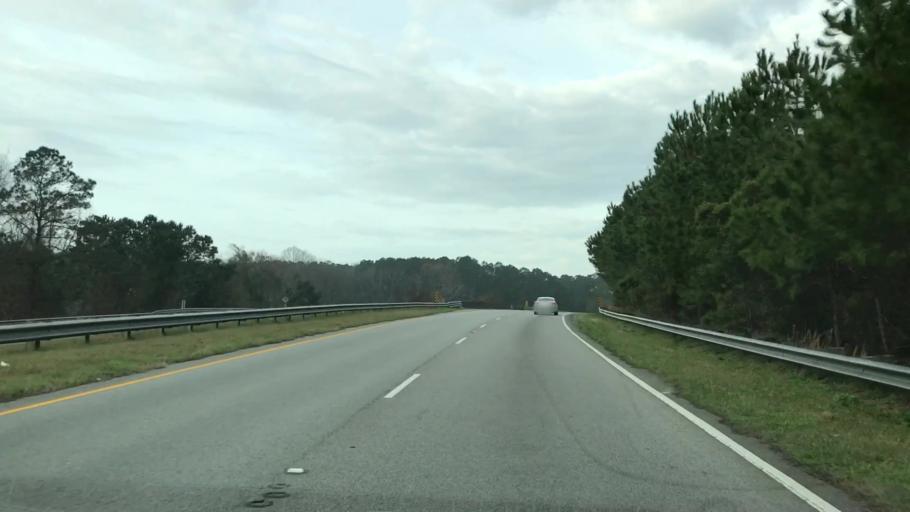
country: US
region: South Carolina
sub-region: Hampton County
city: Yemassee
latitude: 32.6017
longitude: -80.7960
